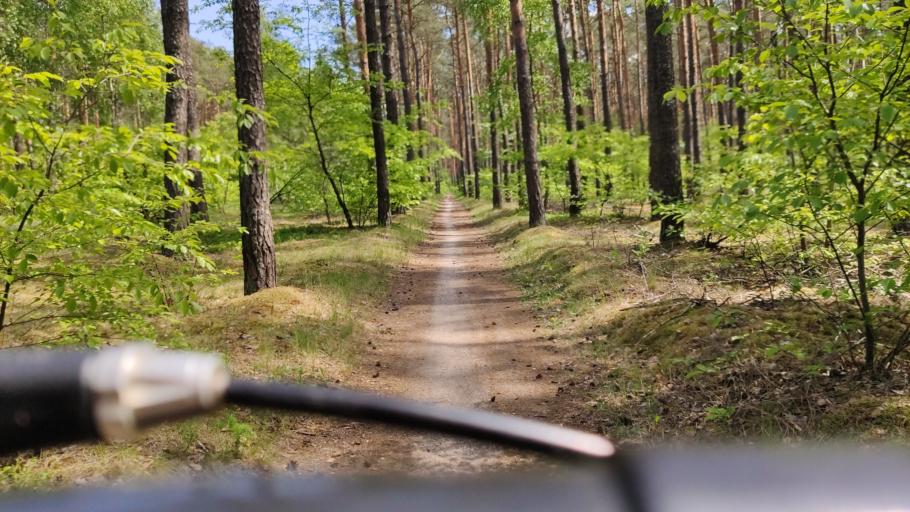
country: PL
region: Kujawsko-Pomorskie
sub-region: Wloclawek
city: Wloclawek
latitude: 52.6339
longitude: 19.1287
